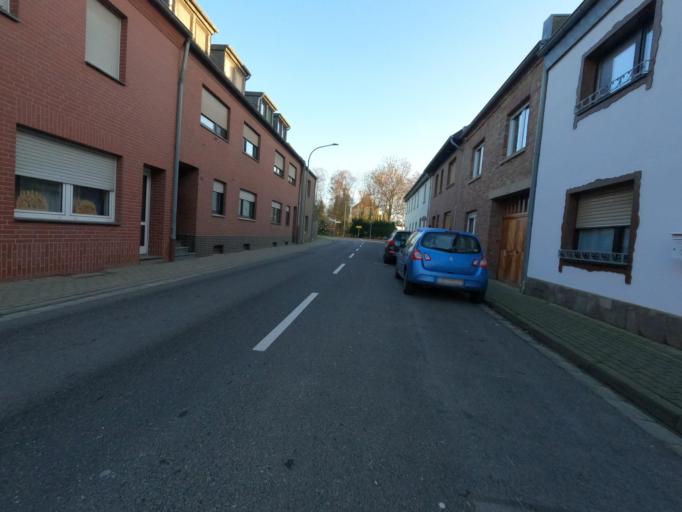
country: DE
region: North Rhine-Westphalia
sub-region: Regierungsbezirk Koln
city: Titz
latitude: 50.9848
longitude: 6.4357
